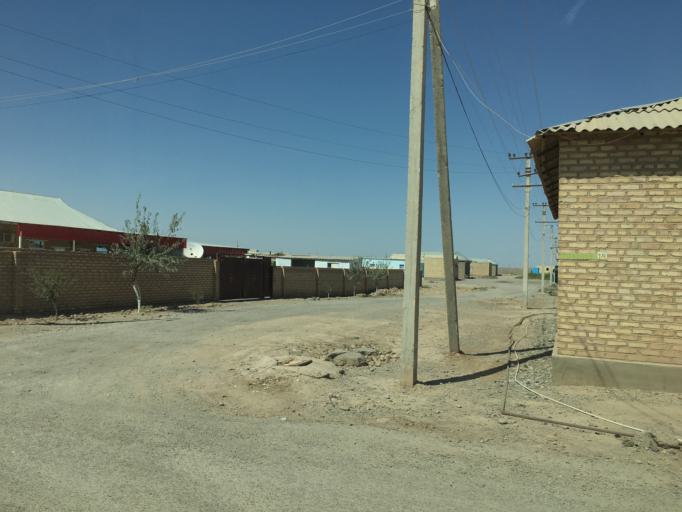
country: IR
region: Razavi Khorasan
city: Sarakhs
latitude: 36.5435
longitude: 61.2046
